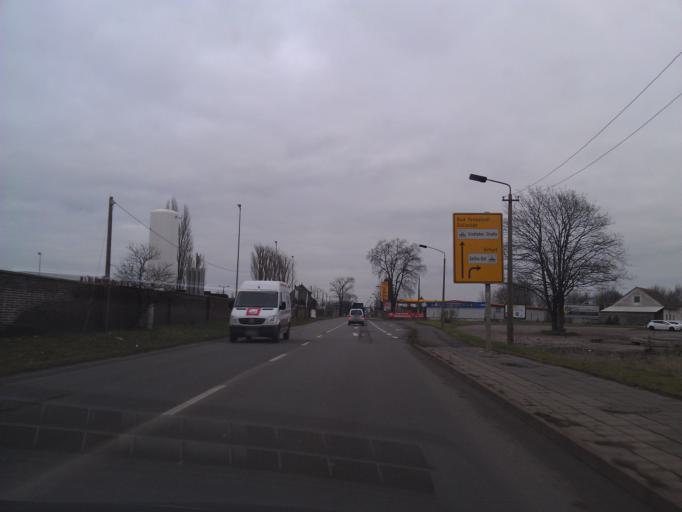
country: DE
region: Thuringia
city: Gotha
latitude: 50.9625
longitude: 10.7227
